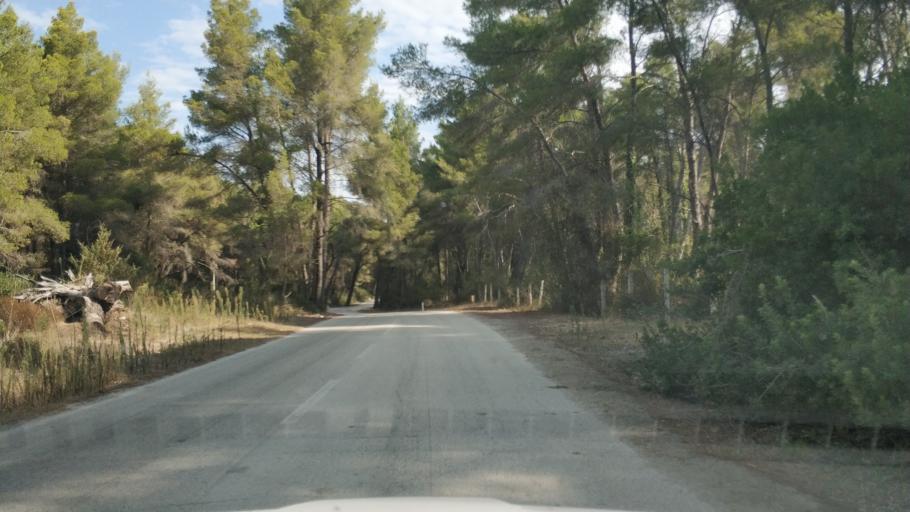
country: AL
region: Fier
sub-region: Rrethi i Lushnjes
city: Divjake
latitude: 40.9794
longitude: 19.4818
